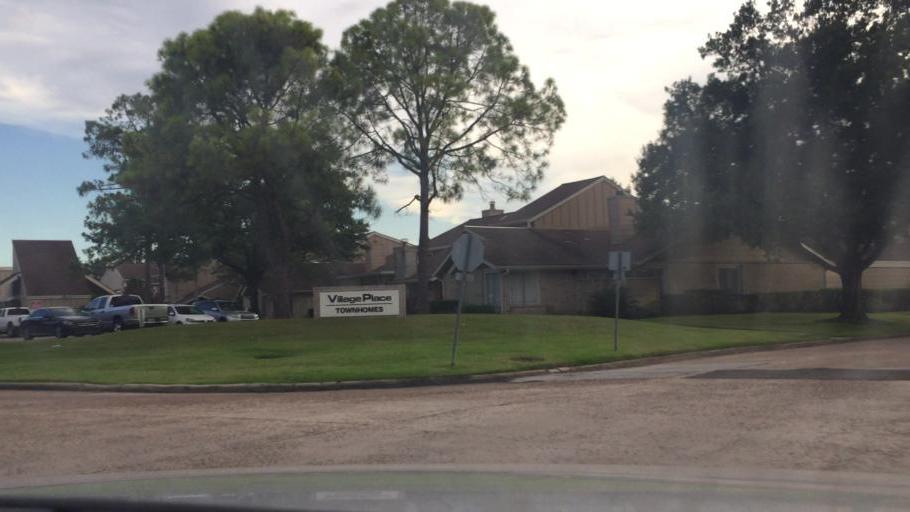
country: US
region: Texas
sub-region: Harris County
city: Bunker Hill Village
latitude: 29.7413
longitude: -95.5813
